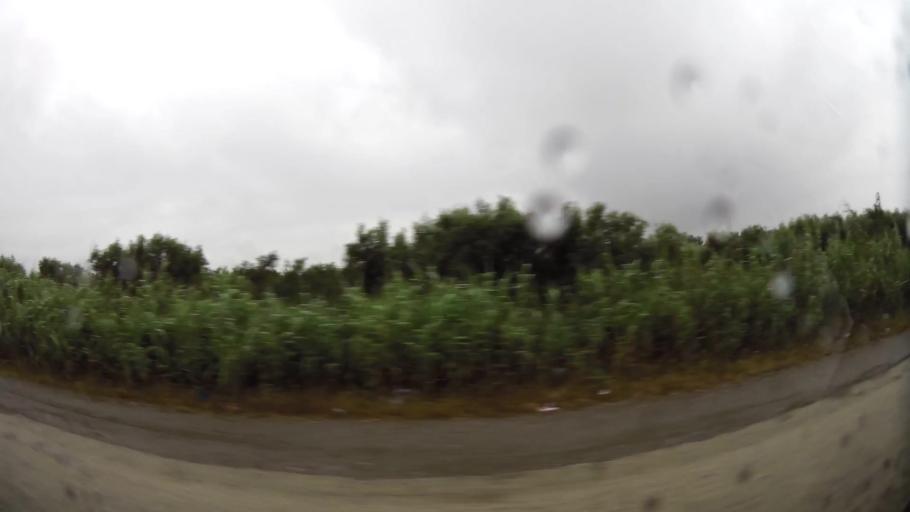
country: MA
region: Taza-Al Hoceima-Taounate
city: Imzourene
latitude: 35.1424
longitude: -3.8068
